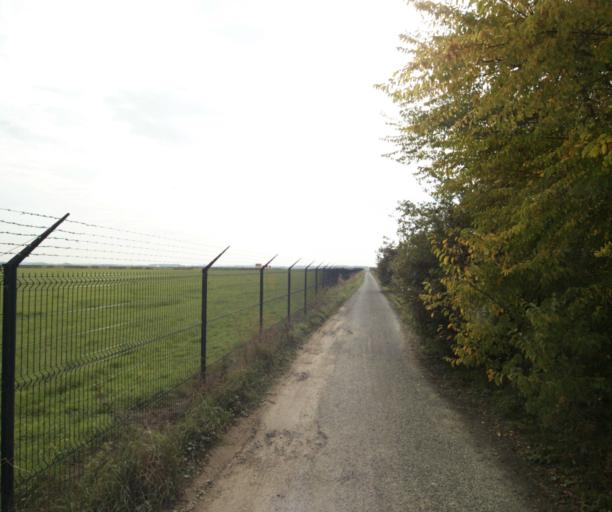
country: FR
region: Nord-Pas-de-Calais
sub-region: Departement du Nord
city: Vendeville
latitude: 50.5640
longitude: 3.0757
